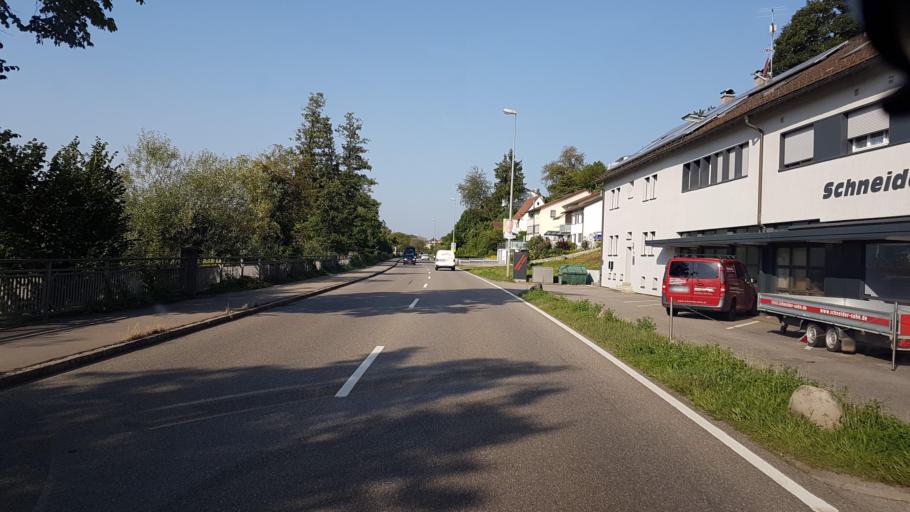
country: DE
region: Baden-Wuerttemberg
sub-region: Freiburg Region
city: Waldshut-Tiengen
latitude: 47.6209
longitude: 8.1991
